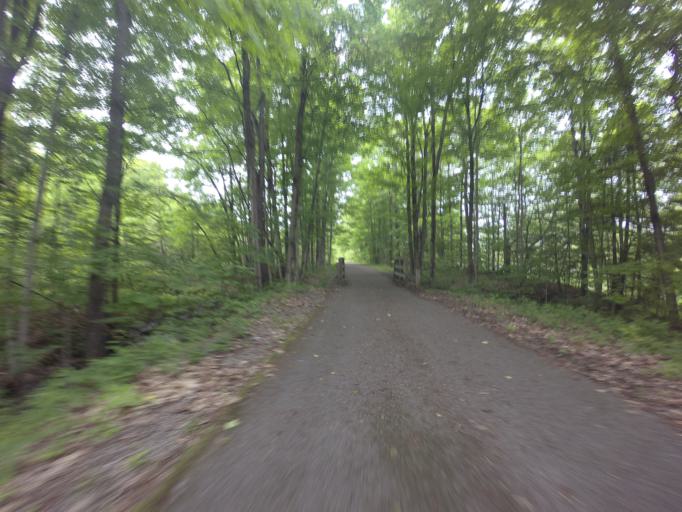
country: US
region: New York
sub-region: Jefferson County
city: Calcium
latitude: 43.9881
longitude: -75.8369
